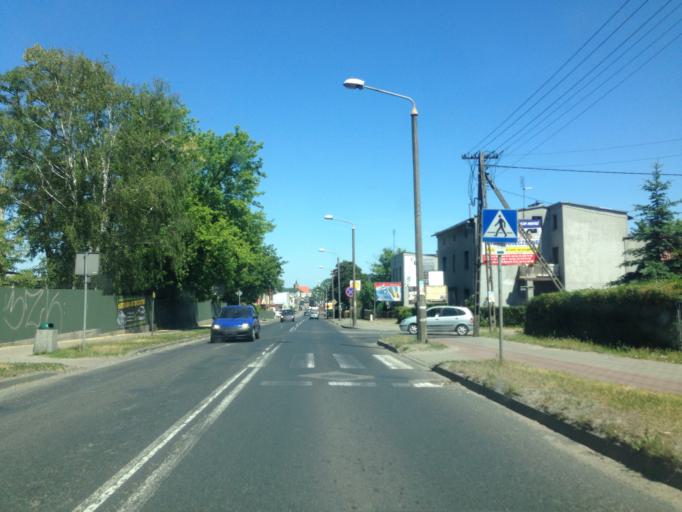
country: PL
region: Kujawsko-Pomorskie
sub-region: Powiat brodnicki
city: Brodnica
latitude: 53.2449
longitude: 19.3968
